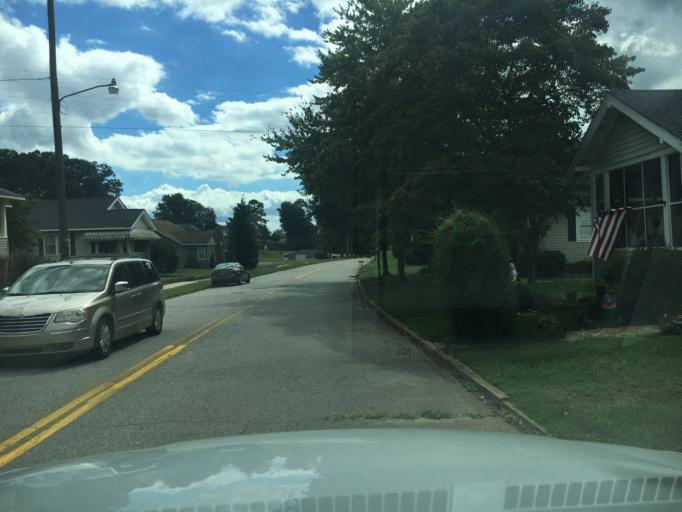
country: US
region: South Carolina
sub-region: Spartanburg County
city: Lyman
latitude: 34.9501
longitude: -82.1274
